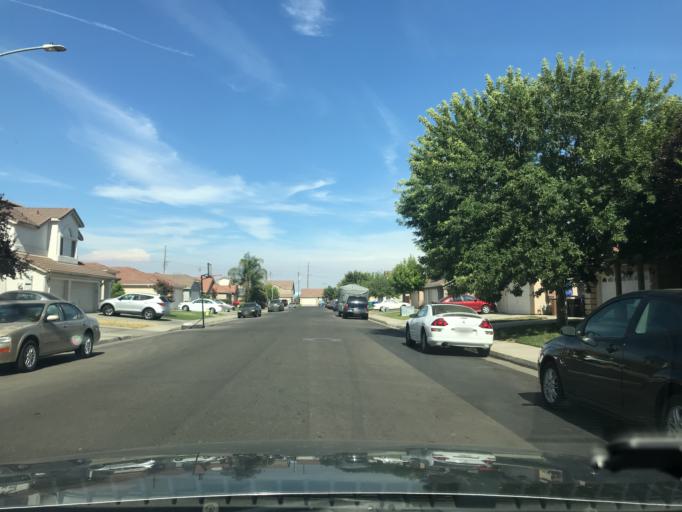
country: US
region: California
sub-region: Merced County
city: Merced
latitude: 37.3281
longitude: -120.5257
